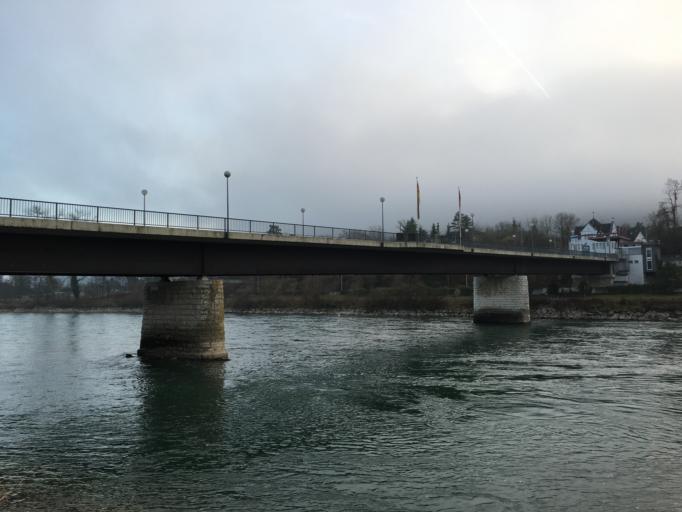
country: CH
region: Aargau
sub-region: Bezirk Zurzach
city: Bad Zurzach
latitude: 47.5868
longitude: 8.3025
